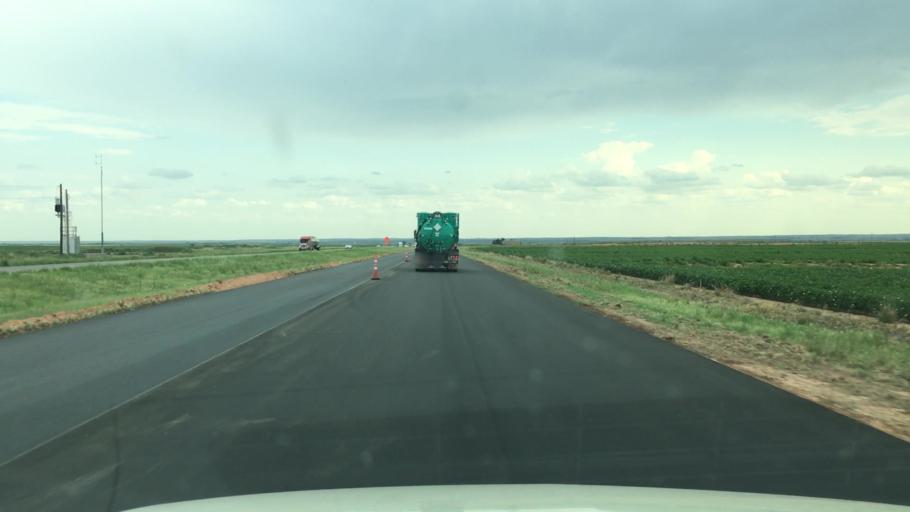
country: US
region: Texas
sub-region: Hall County
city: Memphis
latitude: 34.6267
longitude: -100.4746
